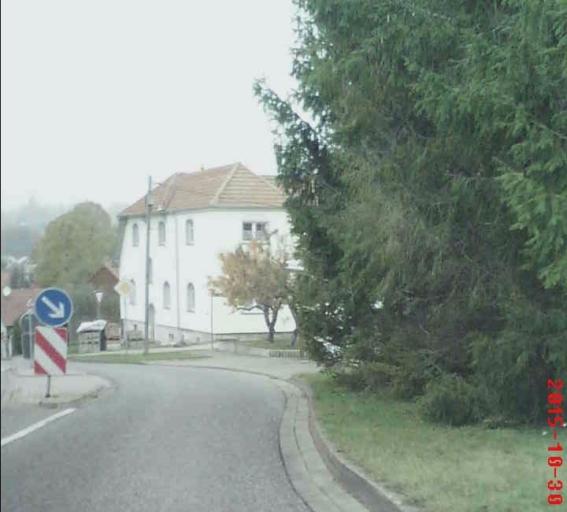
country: DE
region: Thuringia
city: Anrode
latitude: 51.2492
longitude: 10.3498
